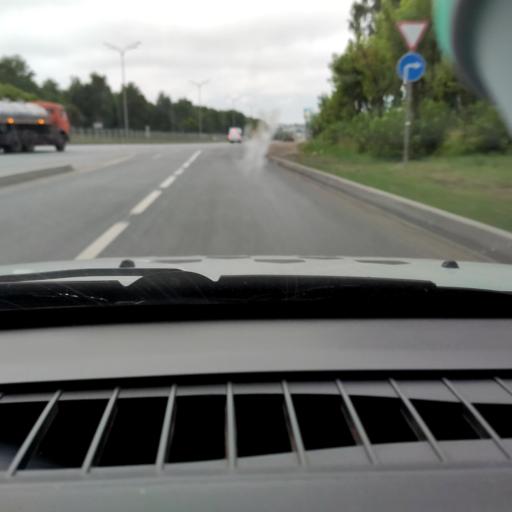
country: RU
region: Tatarstan
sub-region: Tukayevskiy Rayon
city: Naberezhnyye Chelny
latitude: 55.6757
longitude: 52.2862
